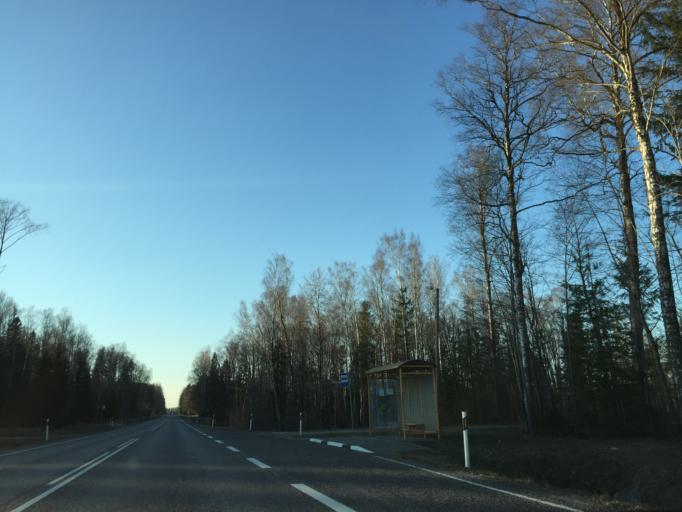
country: EE
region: Ida-Virumaa
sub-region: Johvi vald
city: Johvi
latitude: 59.3237
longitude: 27.4873
